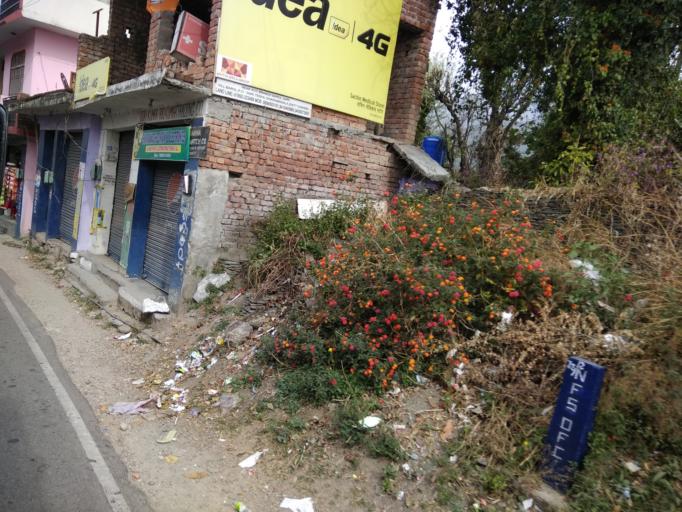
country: IN
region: Himachal Pradesh
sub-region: Kangra
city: Dharmsala
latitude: 32.1972
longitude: 76.3410
